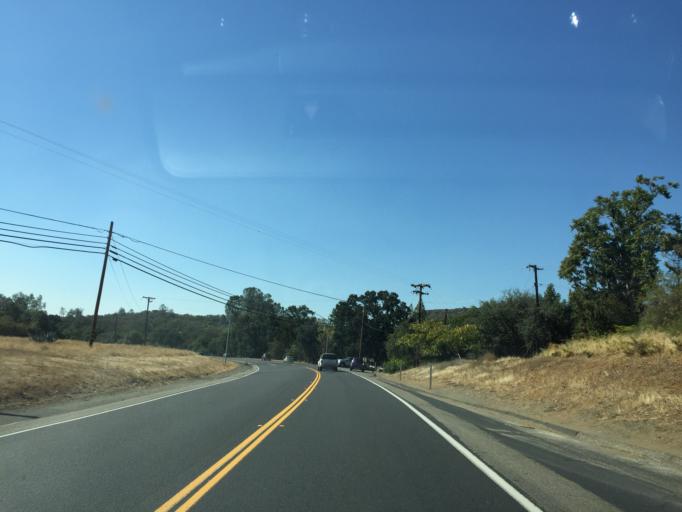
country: US
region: California
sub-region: Tuolumne County
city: Jamestown
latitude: 37.9357
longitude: -120.4423
